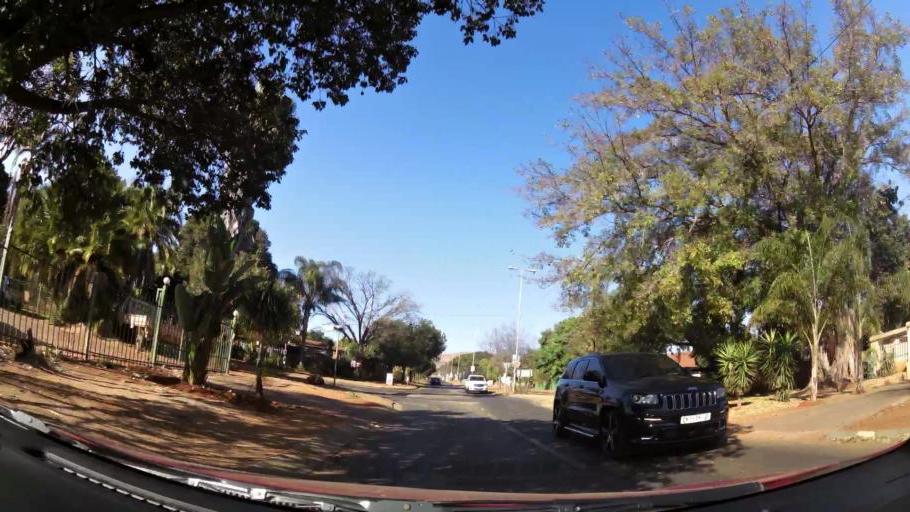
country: ZA
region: Gauteng
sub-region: City of Tshwane Metropolitan Municipality
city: Pretoria
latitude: -25.6692
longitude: 28.1431
